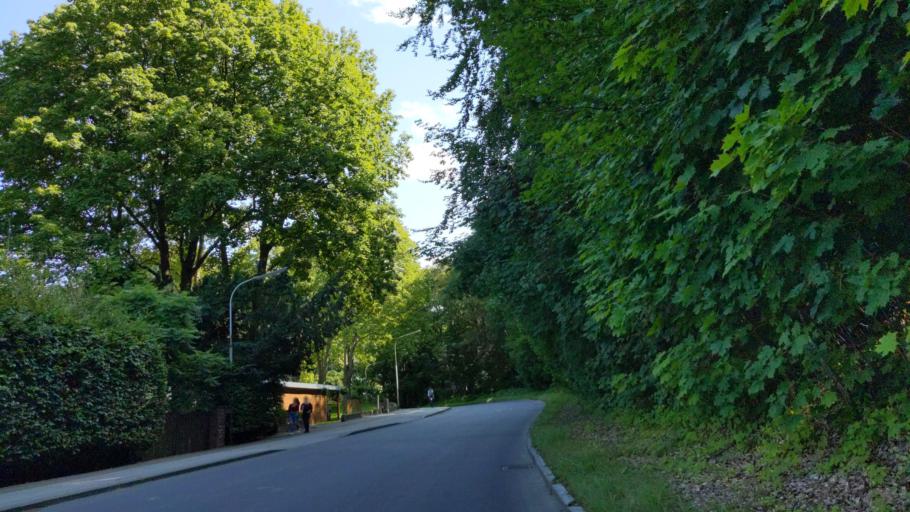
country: DE
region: Schleswig-Holstein
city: Malente
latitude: 54.1638
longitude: 10.5567
